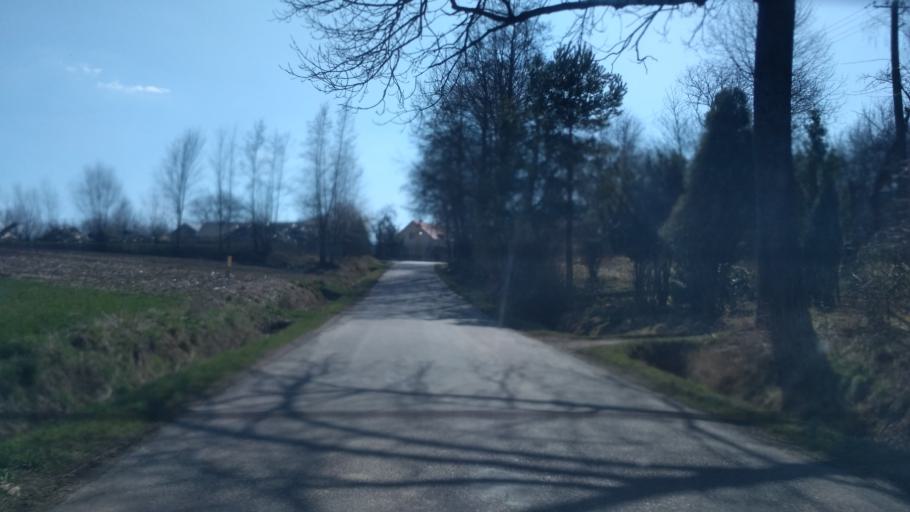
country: PL
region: Subcarpathian Voivodeship
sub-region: Powiat przeworski
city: Pantalowice
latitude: 49.9367
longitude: 22.4450
